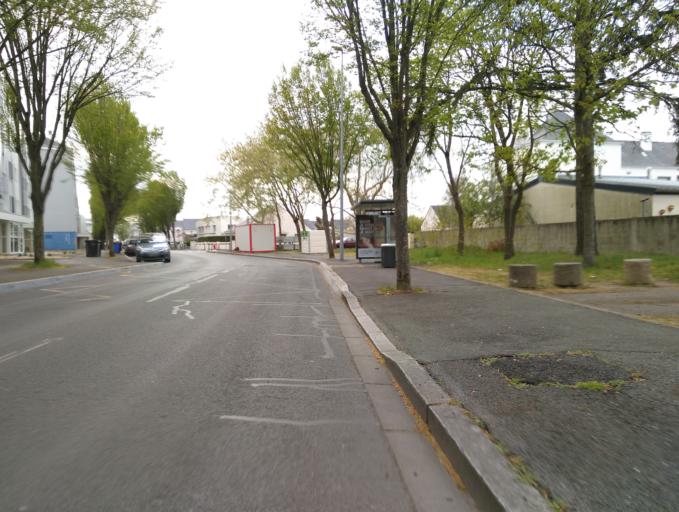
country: FR
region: Pays de la Loire
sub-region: Departement de Maine-et-Loire
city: Angers
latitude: 47.4515
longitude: -0.5349
